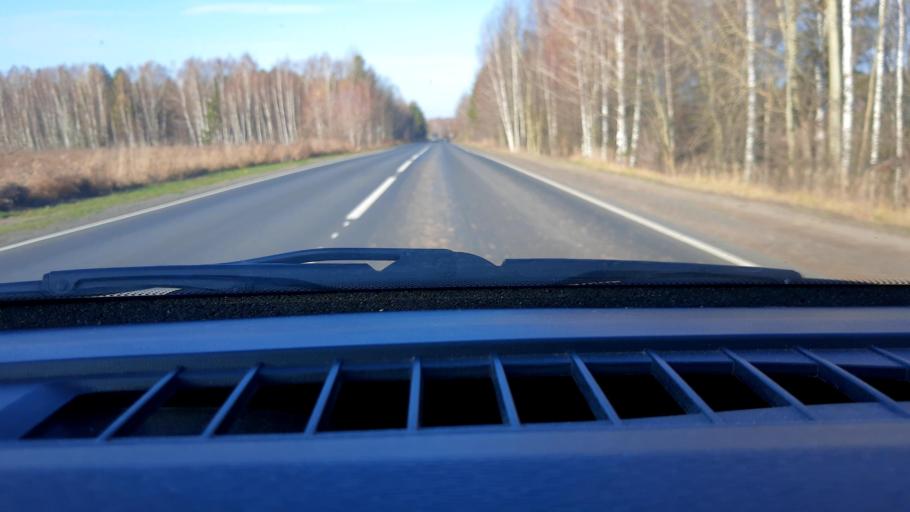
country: RU
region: Nizjnij Novgorod
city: Lukino
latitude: 56.5448
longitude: 43.7601
